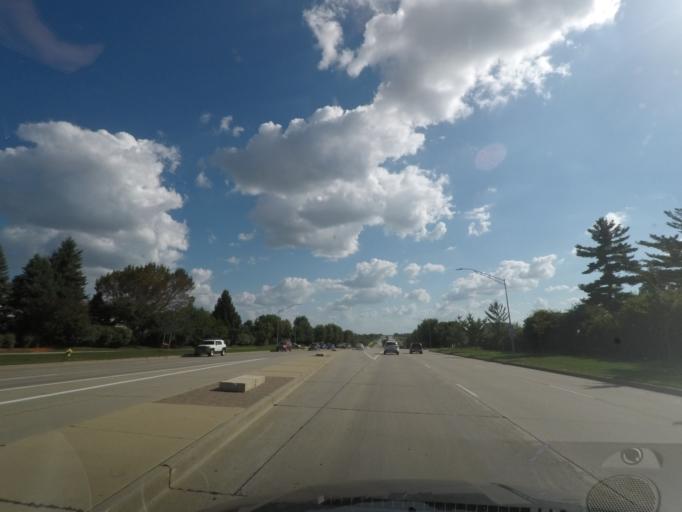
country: US
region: Iowa
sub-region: Dallas County
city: Waukee
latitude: 41.5795
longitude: -93.8093
